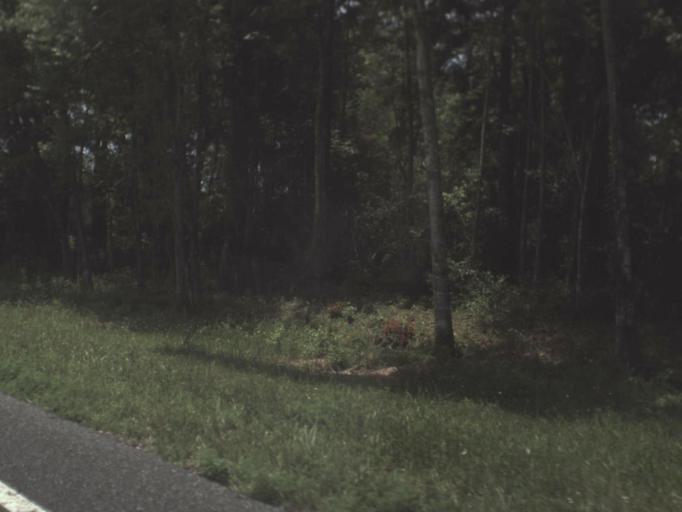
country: US
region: Florida
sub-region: Taylor County
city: Perry
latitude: 29.9548
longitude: -83.4620
